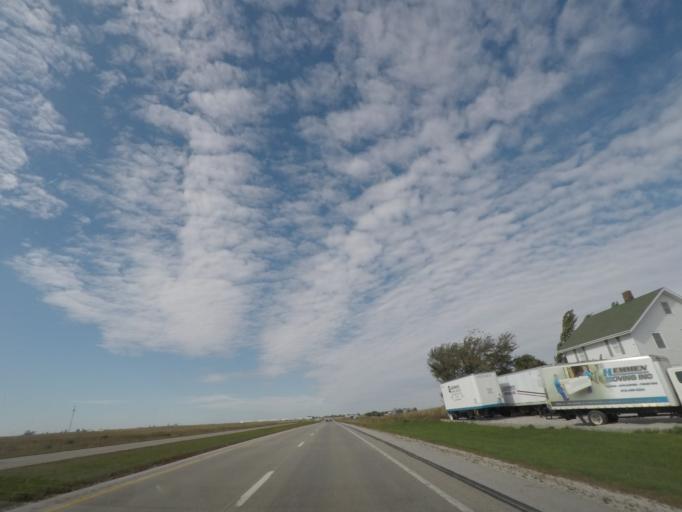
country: US
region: Iowa
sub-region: Story County
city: Ames
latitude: 42.0233
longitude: -93.7460
